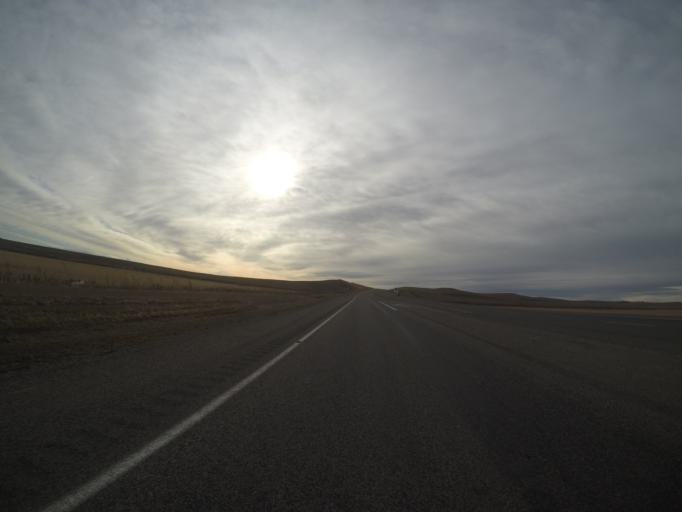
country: US
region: Montana
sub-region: Yellowstone County
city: Laurel
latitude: 45.6088
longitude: -108.8219
